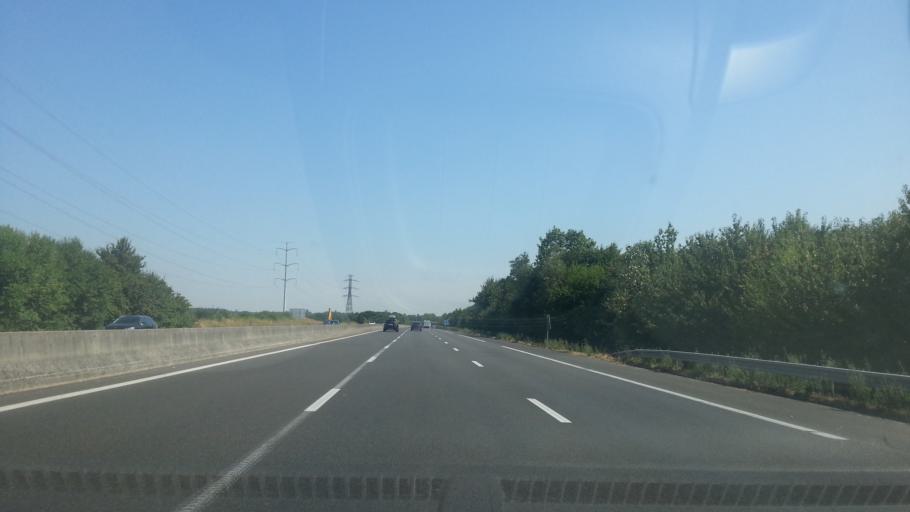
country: FR
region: Centre
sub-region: Departement du Loiret
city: Meung-sur-Loire
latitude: 47.8416
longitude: 1.6757
